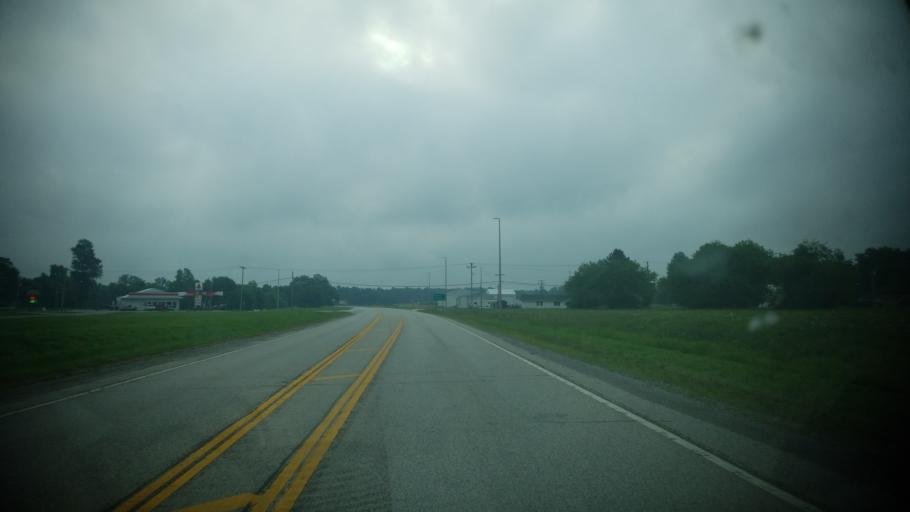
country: US
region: Illinois
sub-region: Clay County
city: Flora
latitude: 38.6791
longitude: -88.3562
